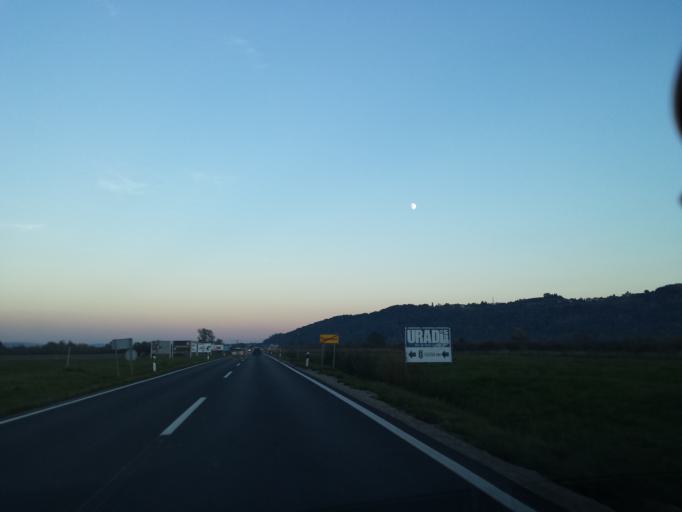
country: HR
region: Zagrebacka
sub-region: Grad Samobor
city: Samobor
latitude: 45.7984
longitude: 15.7385
